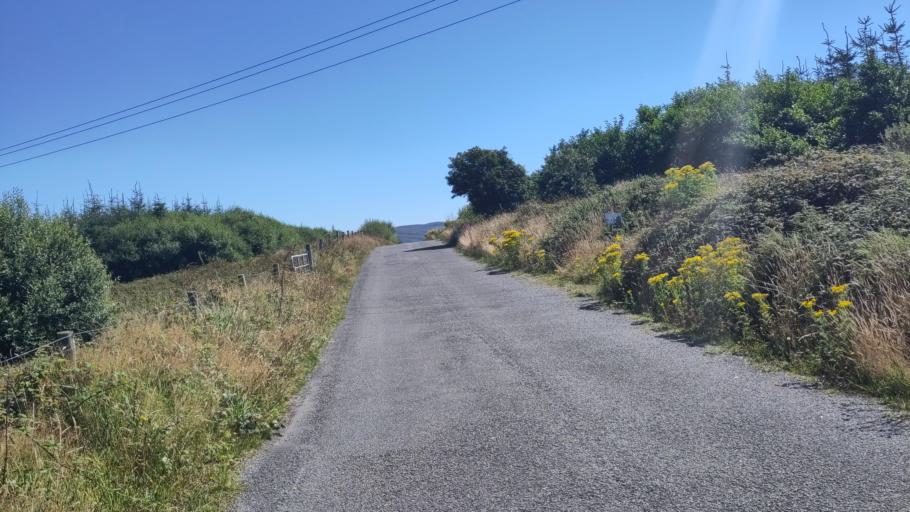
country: IE
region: Munster
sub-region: Ciarrai
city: Kenmare
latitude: 51.6674
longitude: -9.9119
